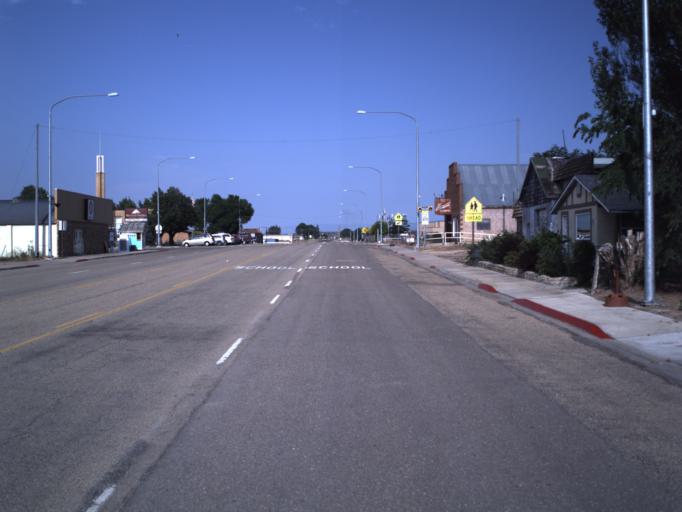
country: US
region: Utah
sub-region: Duchesne County
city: Duchesne
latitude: 40.3594
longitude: -110.2864
